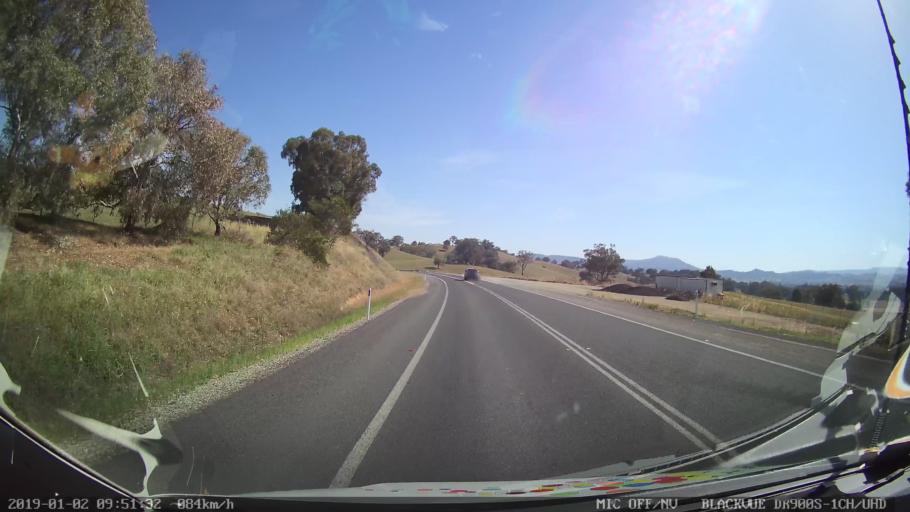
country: AU
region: New South Wales
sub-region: Tumut Shire
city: Tumut
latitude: -35.2720
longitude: 148.2114
